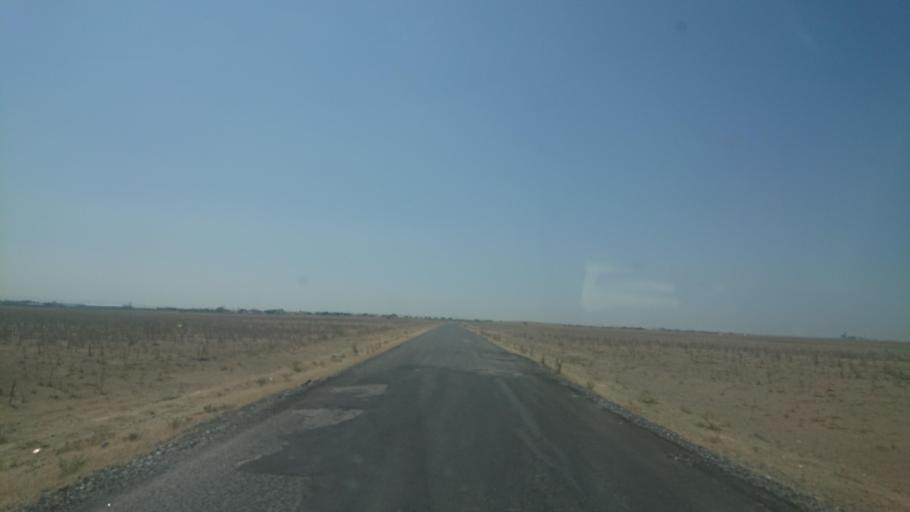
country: TR
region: Aksaray
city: Yesilova
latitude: 38.3045
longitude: 33.7335
